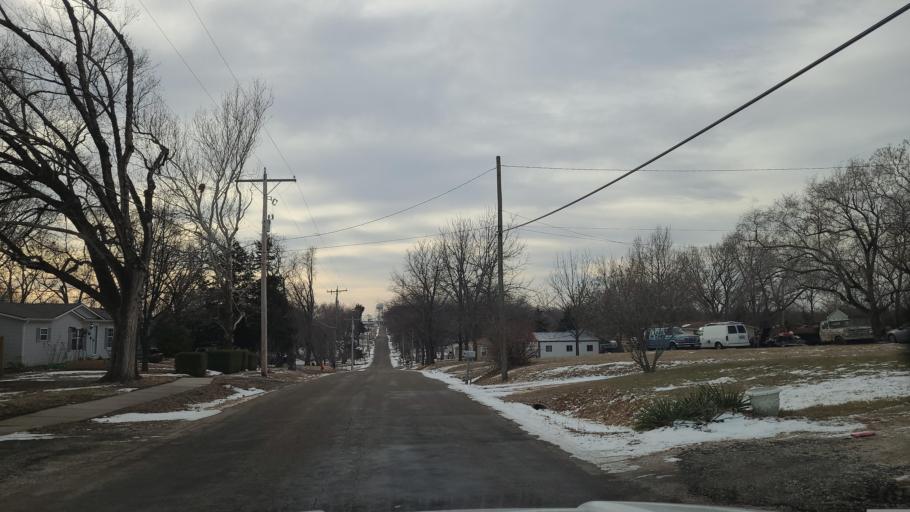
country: US
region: Kansas
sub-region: Douglas County
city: Lawrence
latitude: 39.0435
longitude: -95.3971
